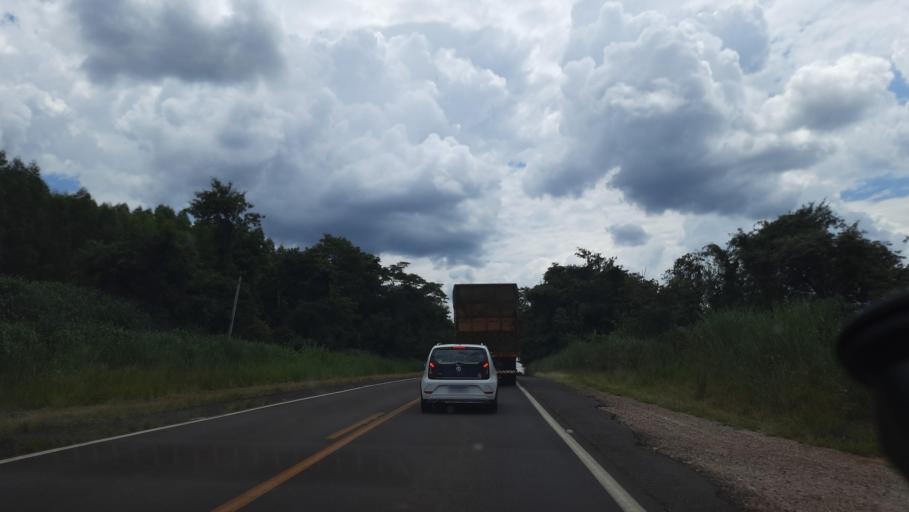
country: BR
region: Sao Paulo
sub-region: Mococa
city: Mococa
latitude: -21.4566
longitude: -47.1218
